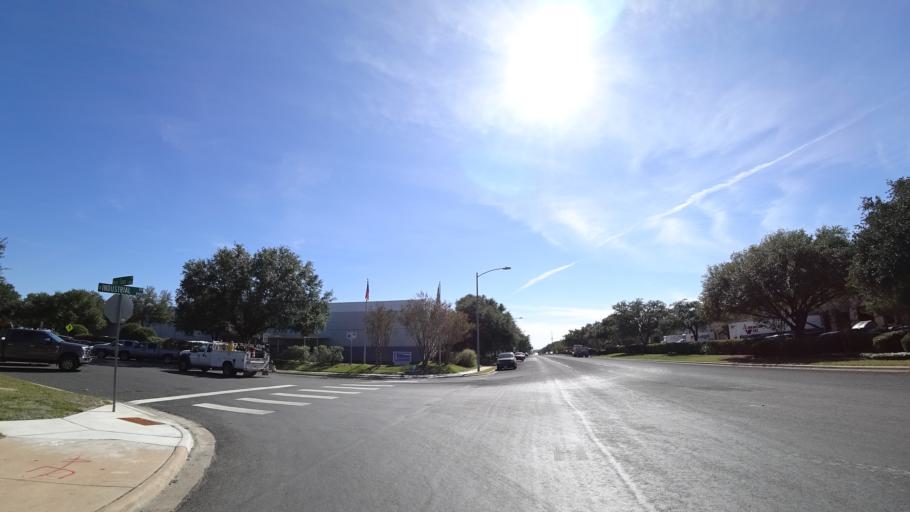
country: US
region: Texas
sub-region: Travis County
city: Austin
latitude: 30.2139
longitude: -97.7411
